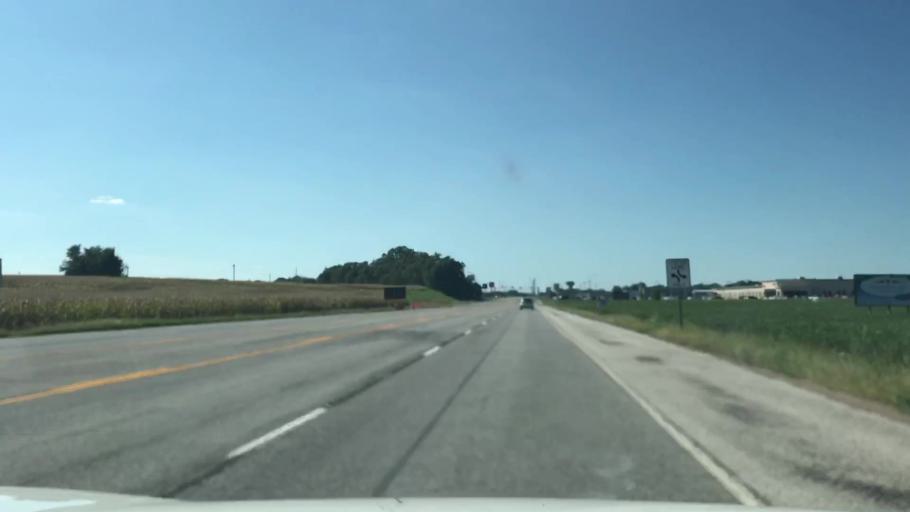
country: US
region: Illinois
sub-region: Madison County
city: Roxana
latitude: 38.8545
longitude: -90.0599
